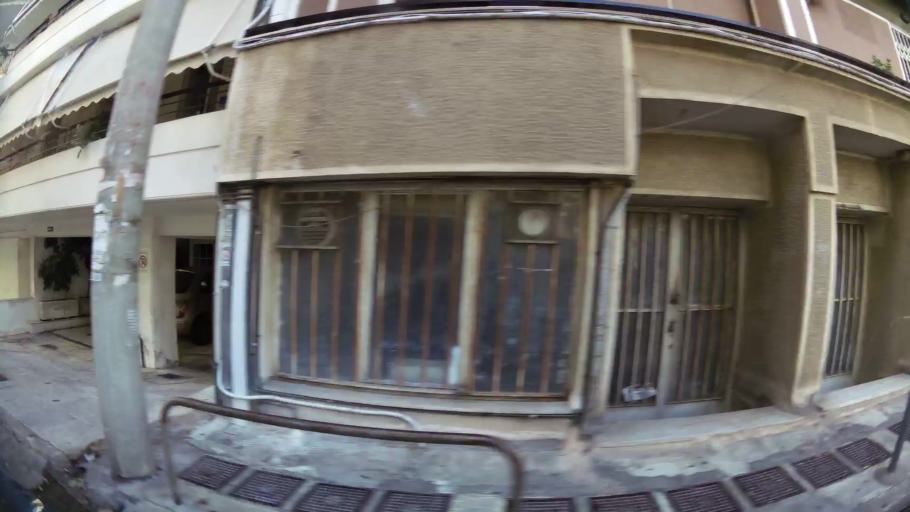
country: GR
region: Attica
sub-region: Nomarchia Athinas
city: Kaisariani
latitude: 37.9742
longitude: 23.7719
